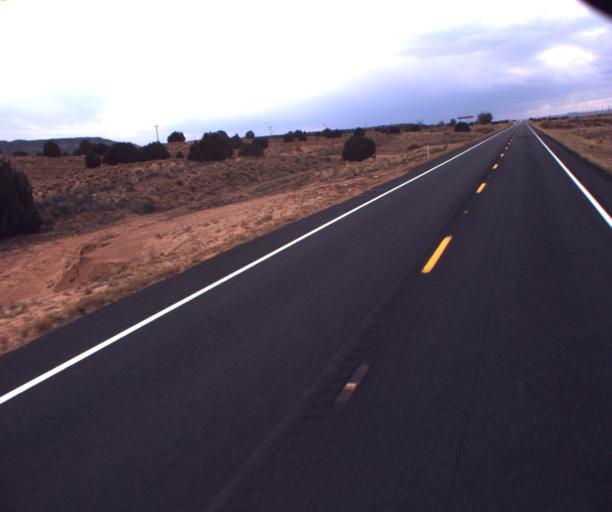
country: US
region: Arizona
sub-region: Coconino County
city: Kaibito
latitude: 36.4150
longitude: -110.8163
